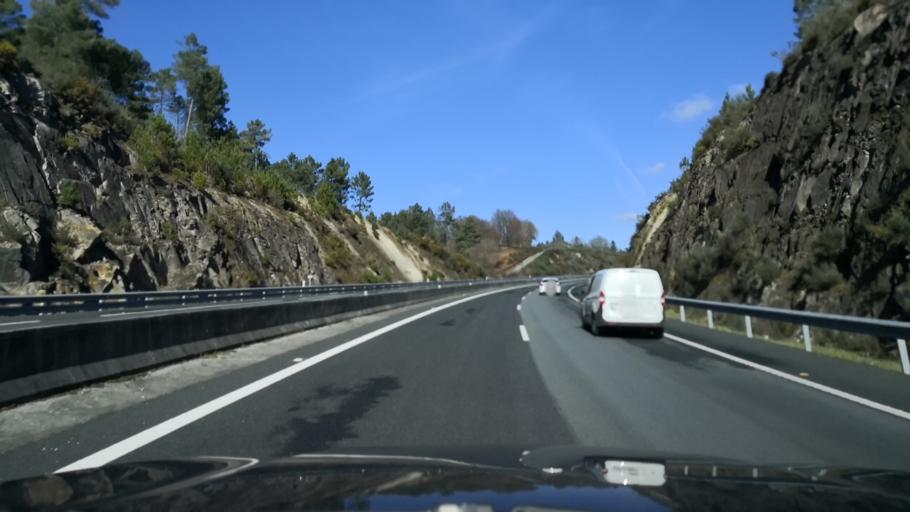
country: ES
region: Galicia
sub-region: Provincia de Ourense
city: Pinor
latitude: 42.5008
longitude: -8.0281
